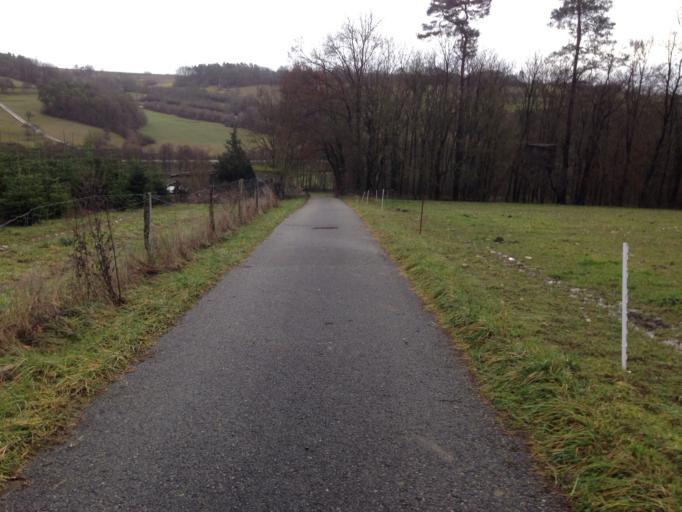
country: DE
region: Baden-Wuerttemberg
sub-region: Karlsruhe Region
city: Limbach
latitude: 49.4044
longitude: 9.2281
